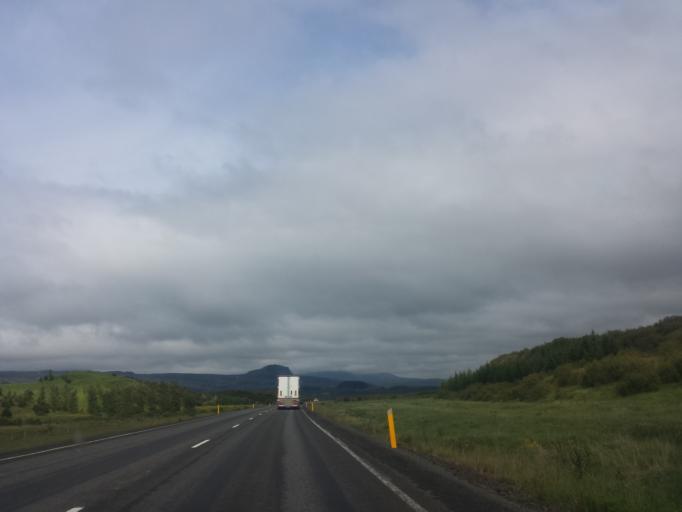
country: IS
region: West
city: Borgarnes
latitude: 64.7332
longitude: -21.5933
